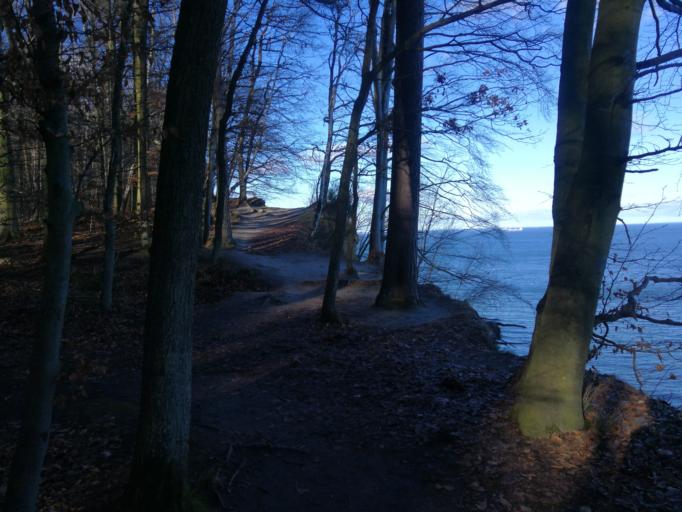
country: PL
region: Pomeranian Voivodeship
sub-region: Sopot
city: Sopot
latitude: 54.4860
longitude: 18.5681
